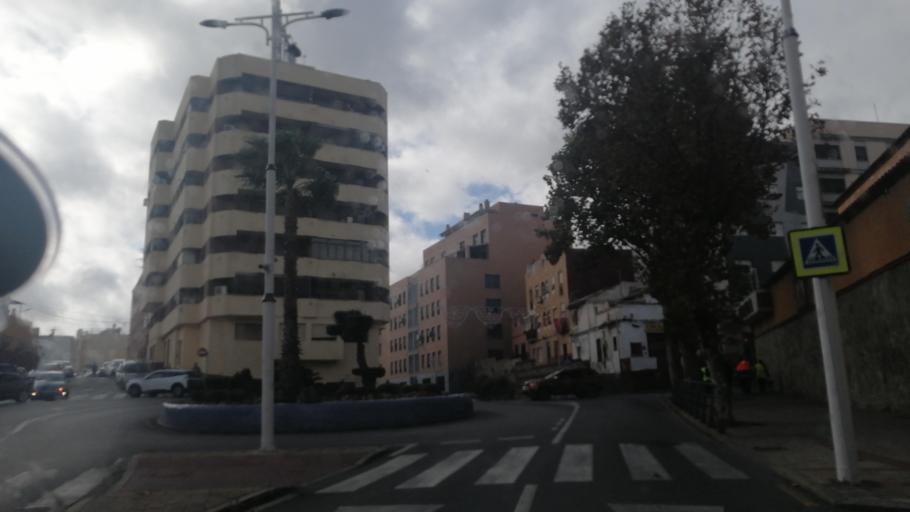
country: ES
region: Ceuta
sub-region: Ceuta
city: Ceuta
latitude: 35.8842
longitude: -5.3274
